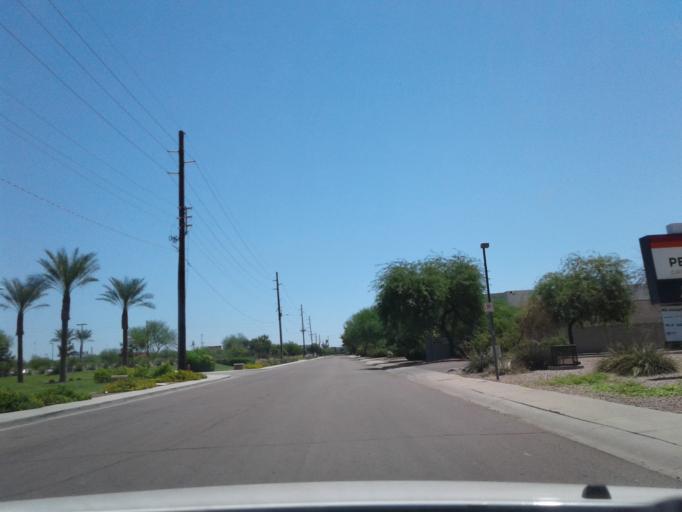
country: US
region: Arizona
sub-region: Maricopa County
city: Guadalupe
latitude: 33.4089
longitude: -112.0114
